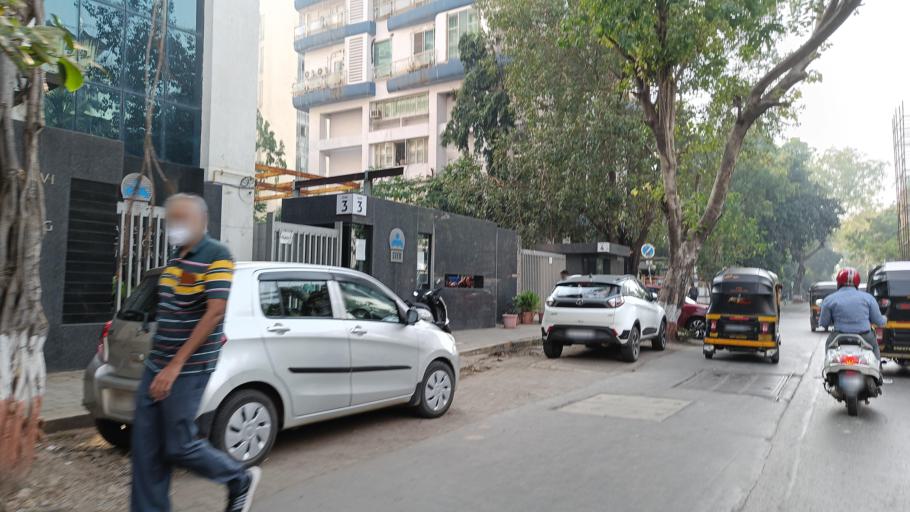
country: IN
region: Maharashtra
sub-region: Mumbai Suburban
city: Mumbai
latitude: 19.1072
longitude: 72.8370
